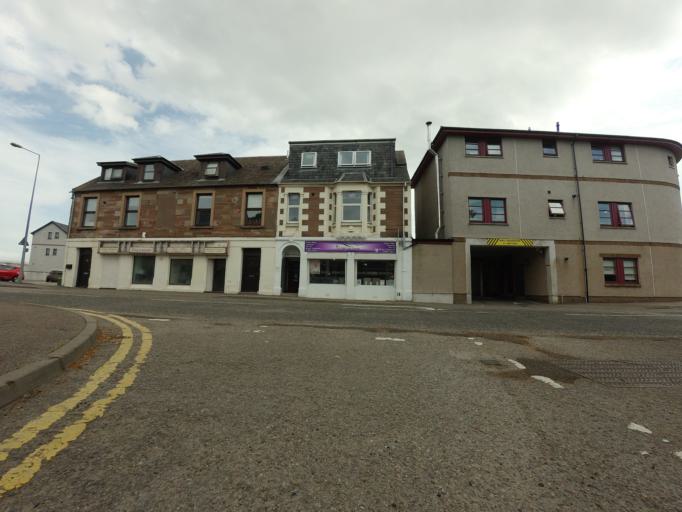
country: GB
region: Scotland
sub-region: Highland
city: Inverness
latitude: 57.4829
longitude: -4.2314
